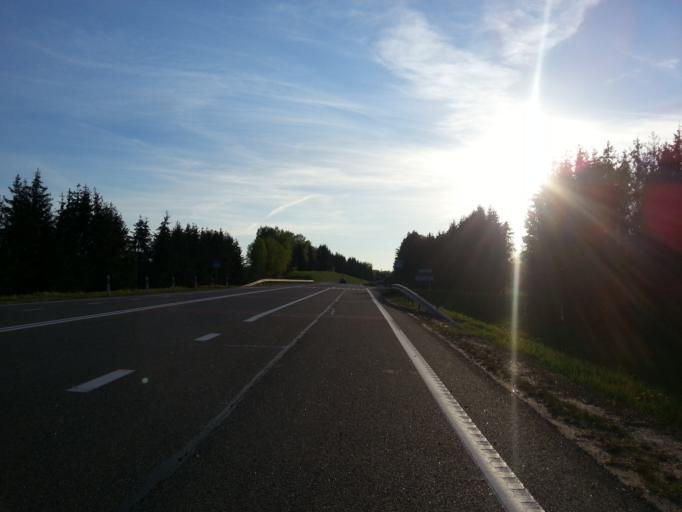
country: BY
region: Minsk
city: Slabada
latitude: 54.0341
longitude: 27.8550
